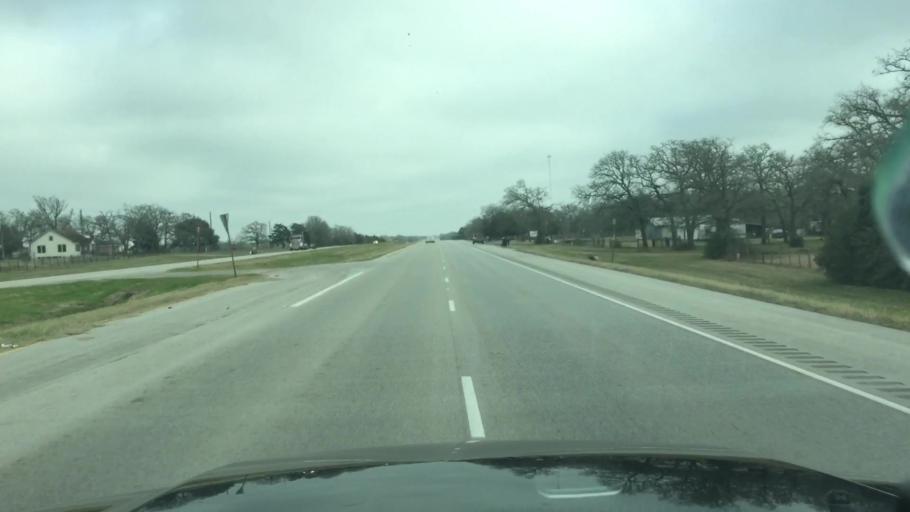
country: US
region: Texas
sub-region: Lee County
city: Giddings
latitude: 30.1461
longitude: -96.7149
